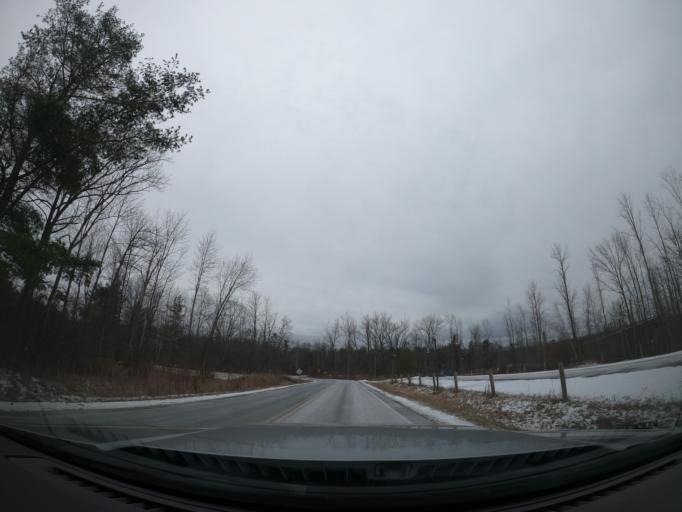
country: US
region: New York
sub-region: Tompkins County
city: Northeast Ithaca
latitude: 42.4812
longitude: -76.4493
